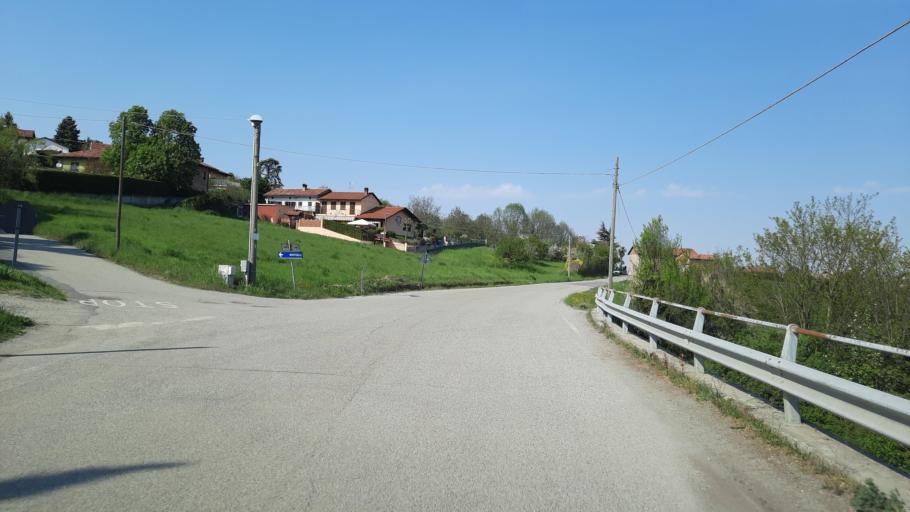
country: IT
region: Piedmont
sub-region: Provincia di Torino
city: Valentino
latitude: 45.1507
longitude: 8.0920
